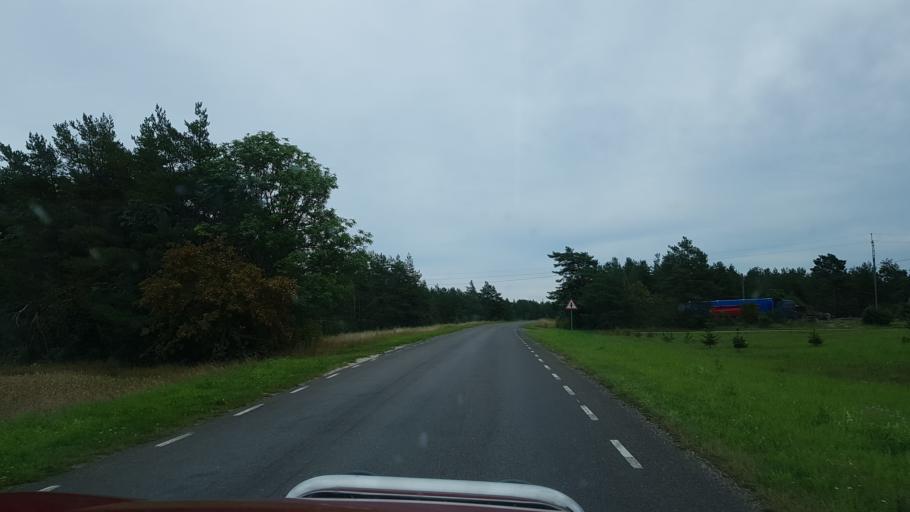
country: EE
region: Laeaene
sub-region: Ridala Parish
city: Uuemoisa
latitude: 58.9349
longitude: 23.7418
